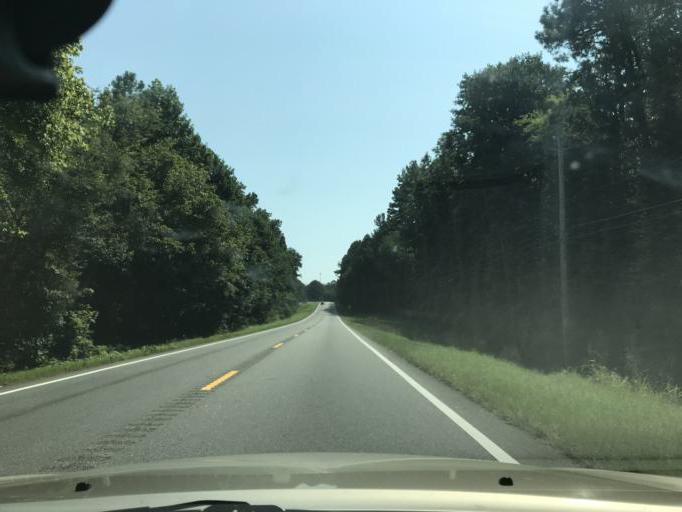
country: US
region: Georgia
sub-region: Hall County
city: Flowery Branch
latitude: 34.2497
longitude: -84.0109
